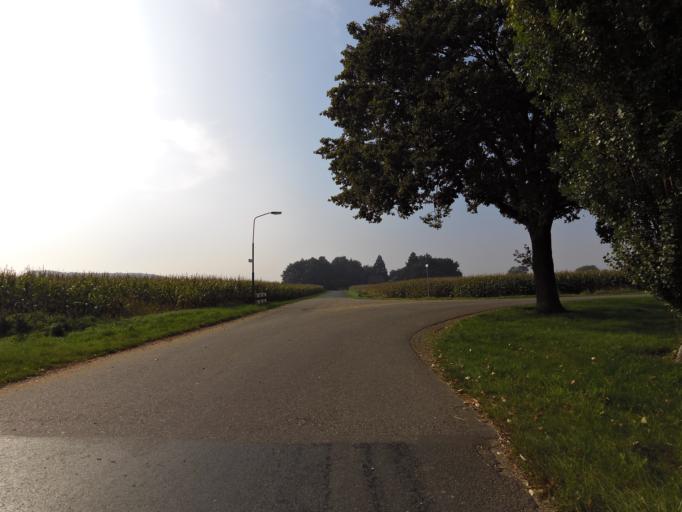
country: NL
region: Gelderland
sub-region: Gemeente Doetinchem
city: Doetinchem
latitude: 51.9446
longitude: 6.2589
